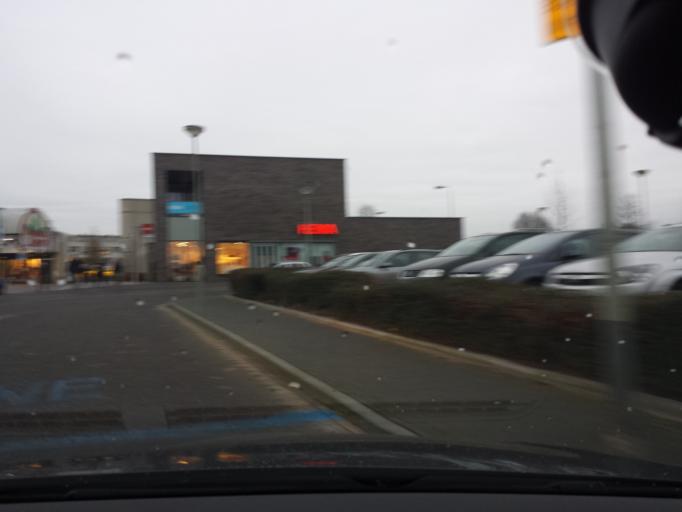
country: NL
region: Limburg
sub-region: Gemeente Heerlen
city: Heerlen
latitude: 50.9062
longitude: 6.0228
